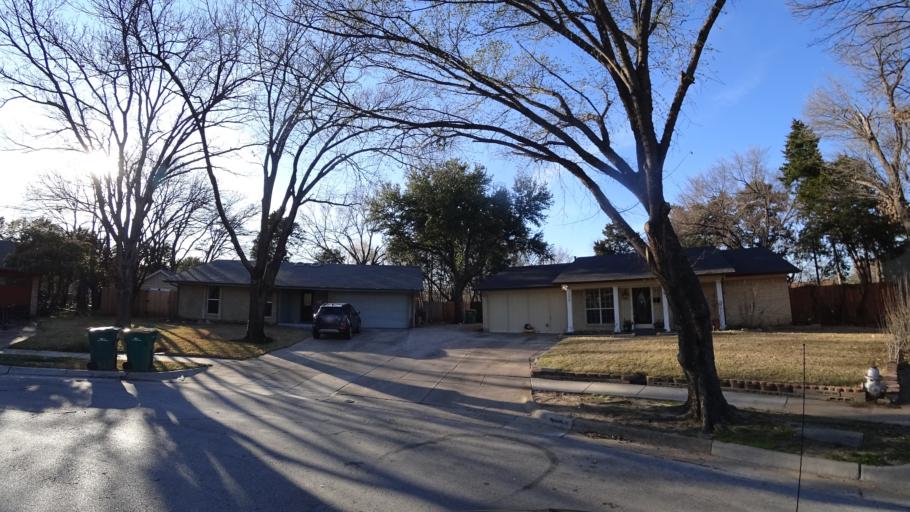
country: US
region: Texas
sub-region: Denton County
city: Lewisville
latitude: 33.0363
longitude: -97.0088
